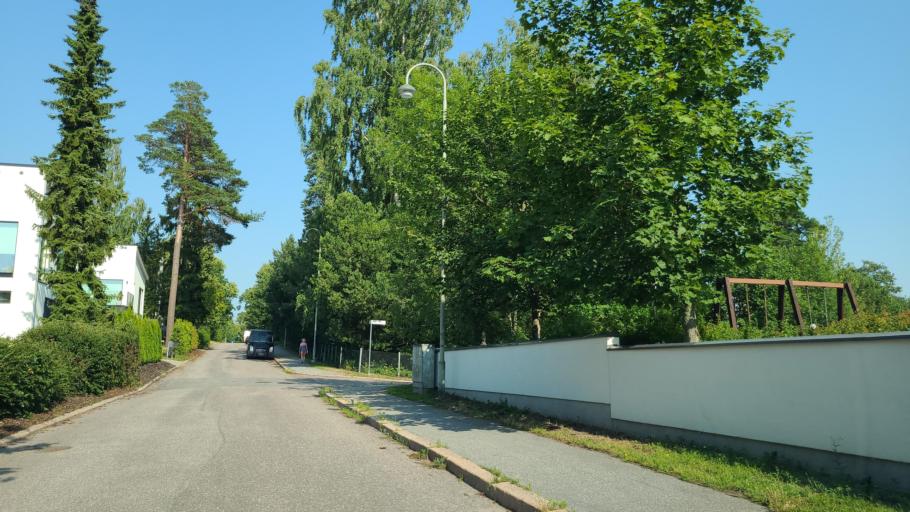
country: FI
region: Uusimaa
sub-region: Helsinki
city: Teekkarikylae
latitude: 60.1843
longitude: 24.8590
